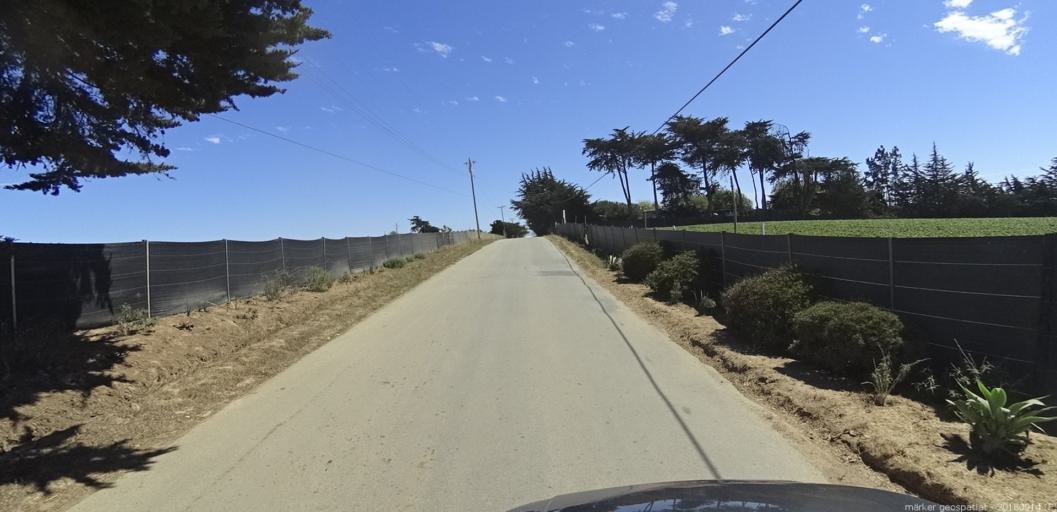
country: US
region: California
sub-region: Monterey County
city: Las Lomas
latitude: 36.8550
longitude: -121.7925
